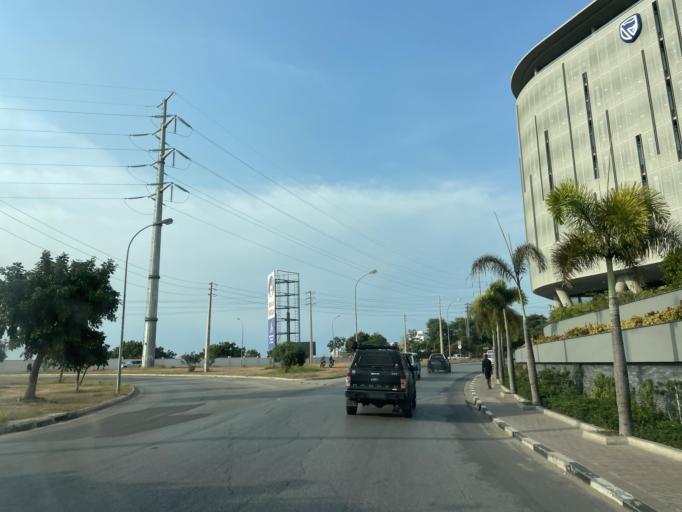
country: AO
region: Luanda
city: Luanda
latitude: -8.9203
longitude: 13.1919
